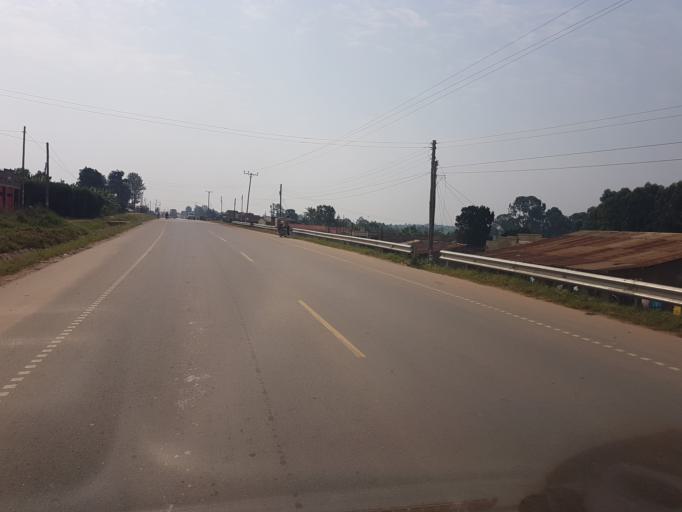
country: UG
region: Western Region
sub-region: Mbarara District
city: Bwizibwera
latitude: -0.6367
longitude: 30.6109
